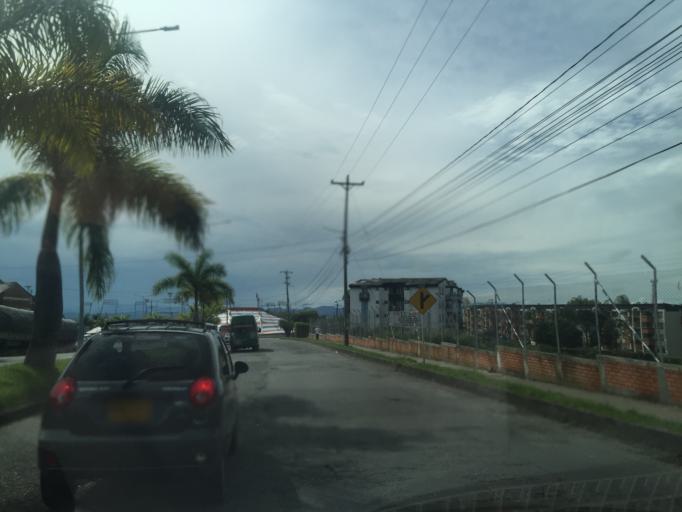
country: CO
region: Quindio
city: Armenia
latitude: 4.5161
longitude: -75.6946
